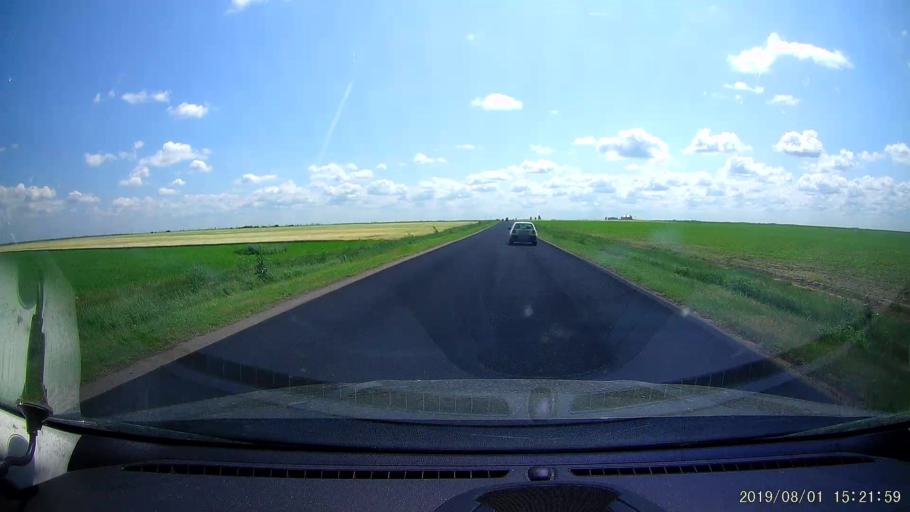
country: RO
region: Braila
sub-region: Comuna Tufesti
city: Tufesti
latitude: 45.0610
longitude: 27.7853
